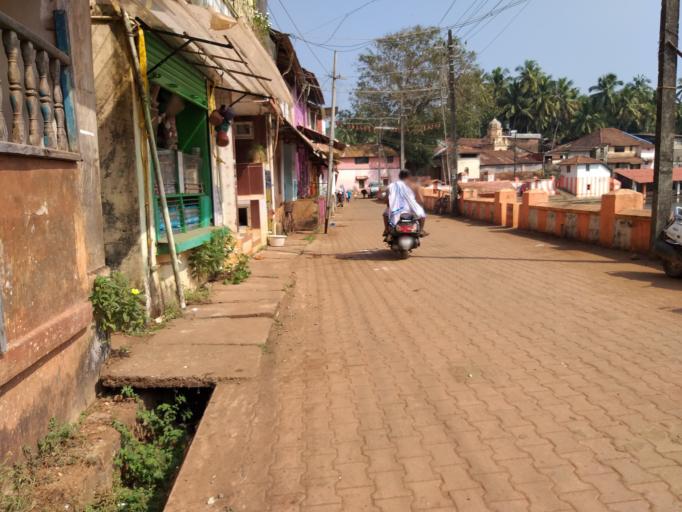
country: IN
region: Karnataka
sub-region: Uttar Kannada
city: Gokarna
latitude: 14.5416
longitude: 74.3196
